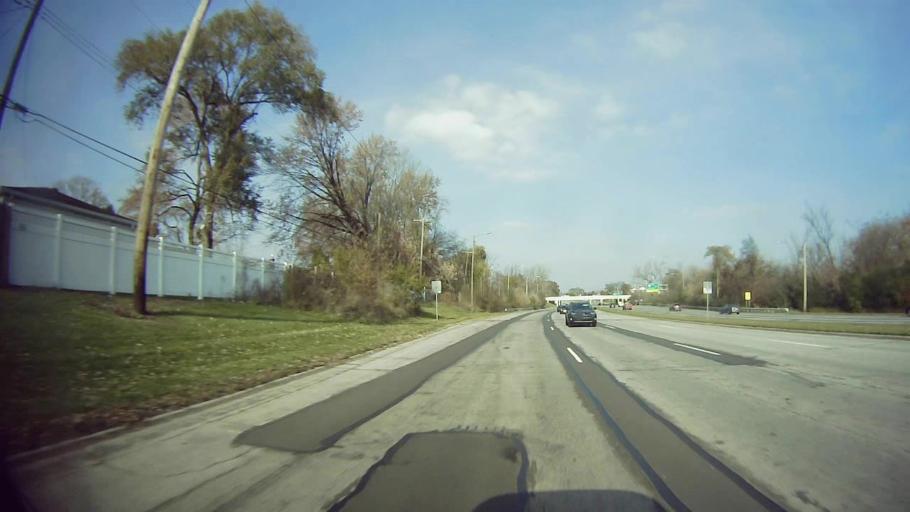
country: US
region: Michigan
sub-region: Wayne County
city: Redford
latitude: 42.4398
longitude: -83.2793
